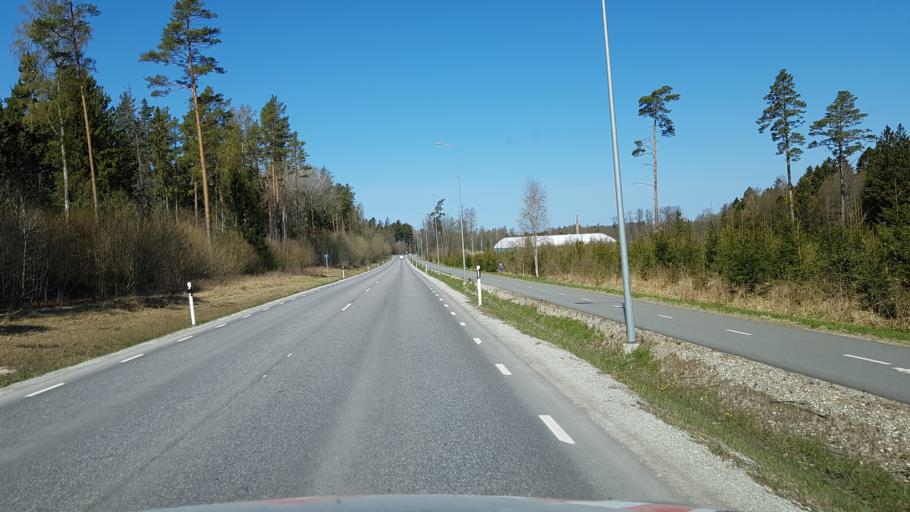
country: EE
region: Harju
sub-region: Viimsi vald
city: Viimsi
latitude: 59.5247
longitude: 24.8850
